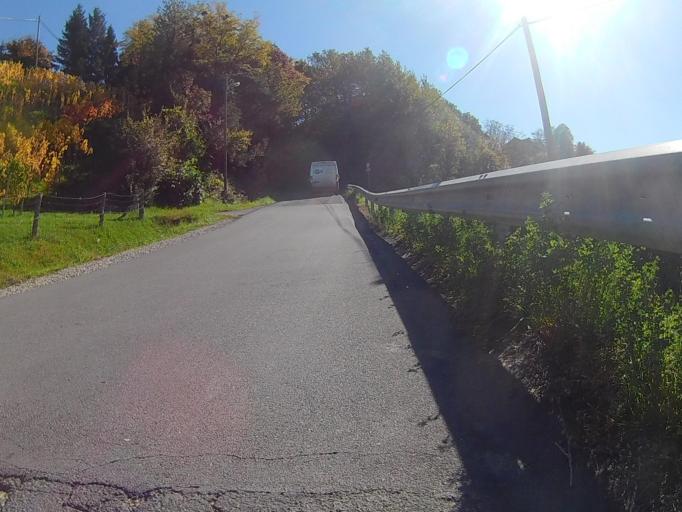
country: SI
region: Duplek
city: Zgornji Duplek
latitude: 46.5380
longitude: 15.7231
